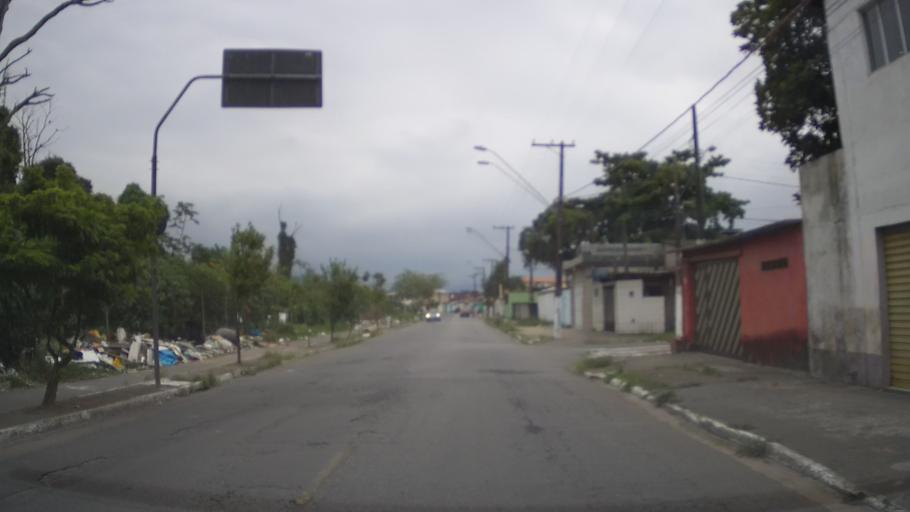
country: BR
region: Sao Paulo
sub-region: Praia Grande
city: Praia Grande
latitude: -24.0028
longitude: -46.4511
